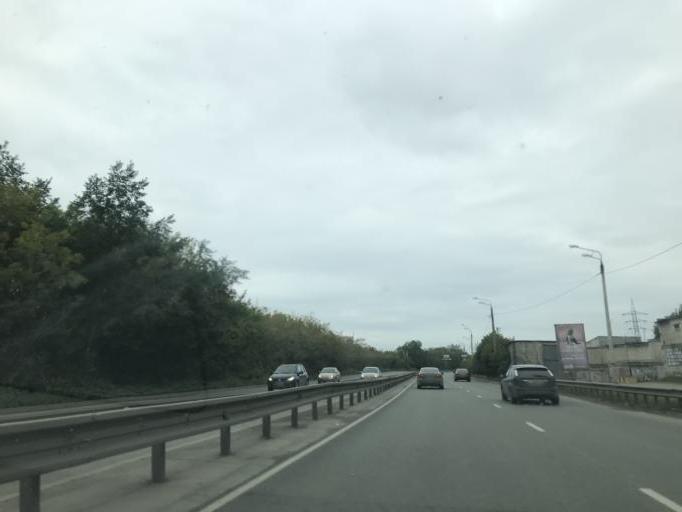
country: RU
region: Chelyabinsk
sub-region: Gorod Chelyabinsk
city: Chelyabinsk
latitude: 55.1734
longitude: 61.4252
